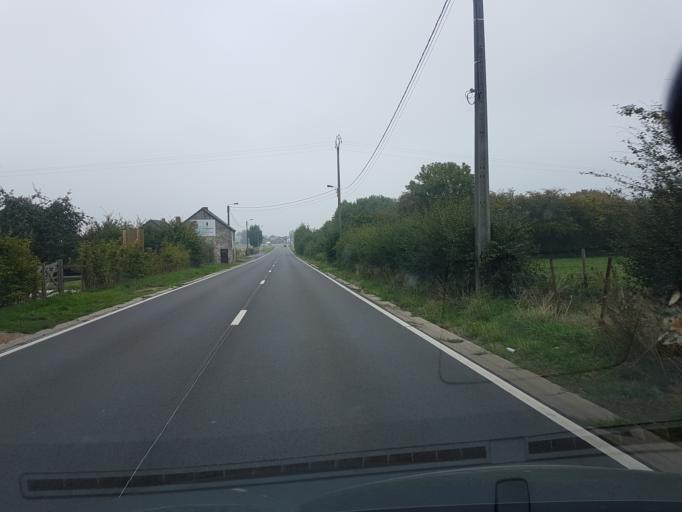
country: BE
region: Wallonia
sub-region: Province de Namur
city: Ohey
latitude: 50.4493
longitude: 5.1167
